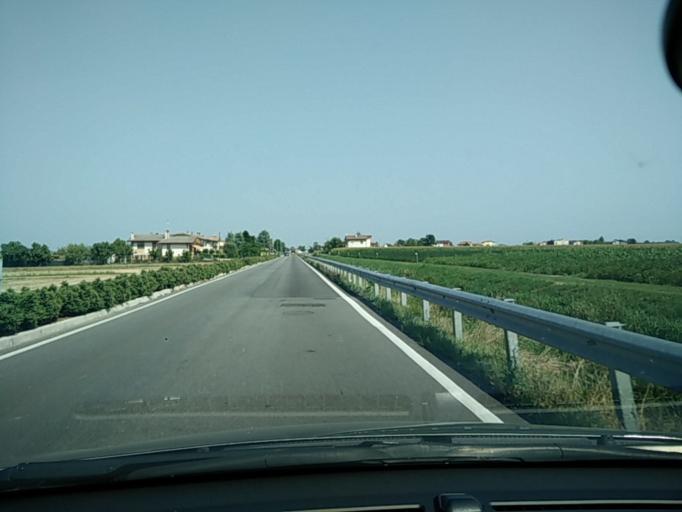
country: IT
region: Veneto
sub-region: Provincia di Venezia
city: Passarella
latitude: 45.6210
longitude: 12.6138
